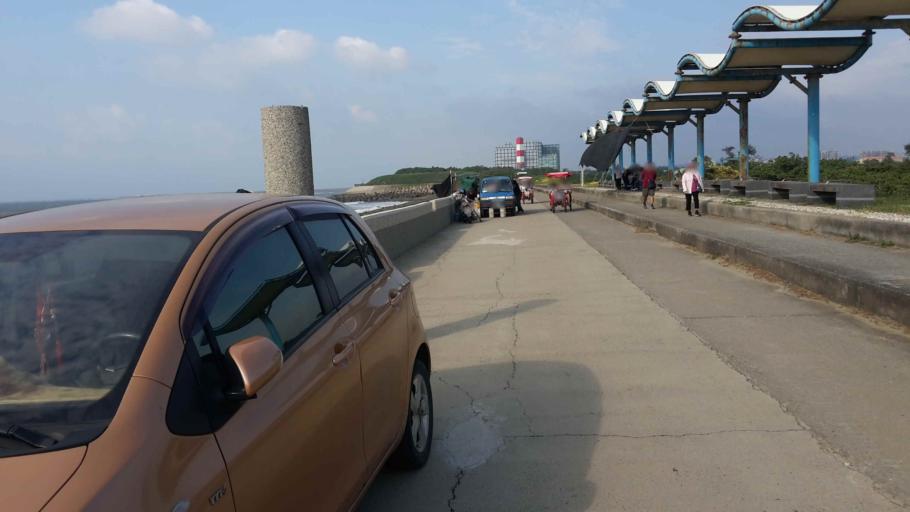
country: TW
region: Taiwan
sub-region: Hsinchu
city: Hsinchu
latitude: 24.8247
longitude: 120.9103
